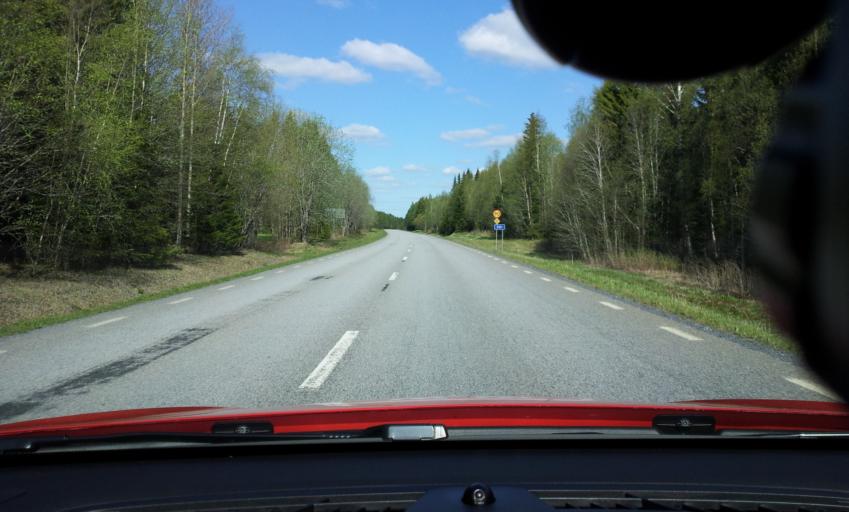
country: SE
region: Jaemtland
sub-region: Krokoms Kommun
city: Valla
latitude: 63.2692
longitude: 13.9576
